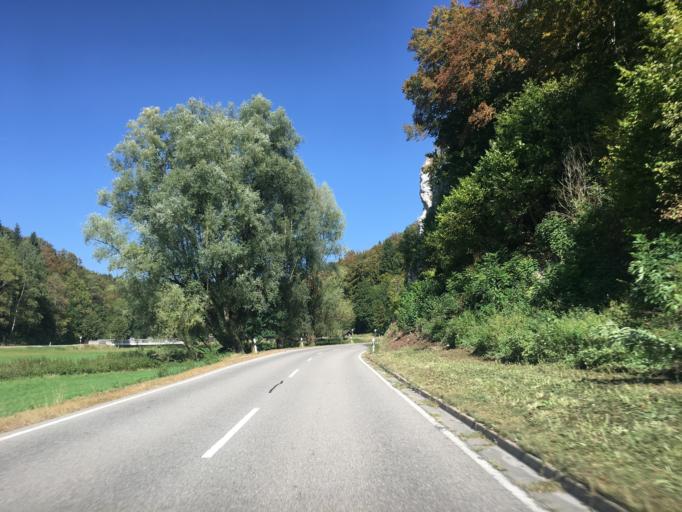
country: DE
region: Baden-Wuerttemberg
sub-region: Tuebingen Region
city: Hayingen
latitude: 48.3084
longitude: 9.4998
